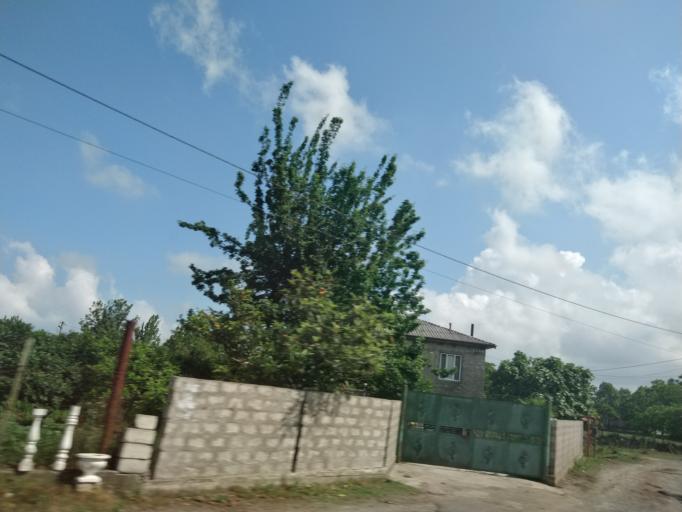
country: GE
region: Ajaria
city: Batumi
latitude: 41.5846
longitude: 41.6033
